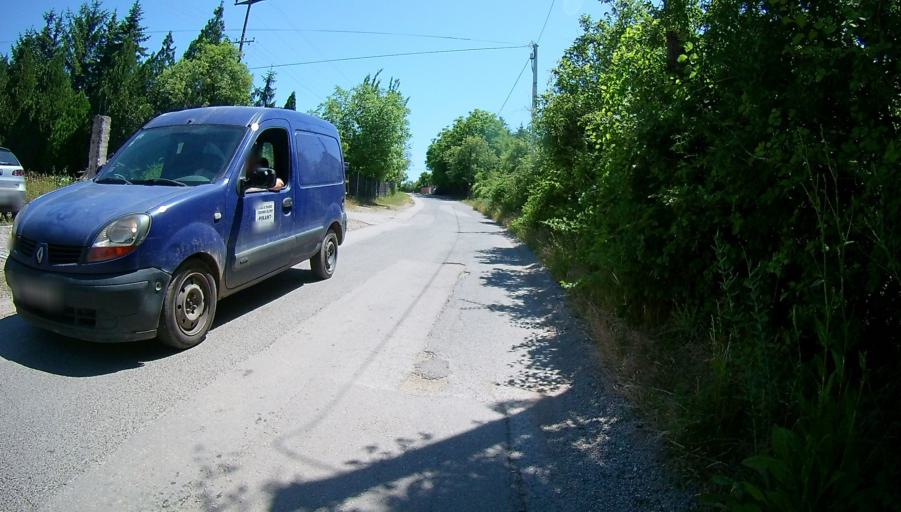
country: RS
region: Central Serbia
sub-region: Nisavski Okrug
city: Nis
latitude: 43.2929
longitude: 21.9000
